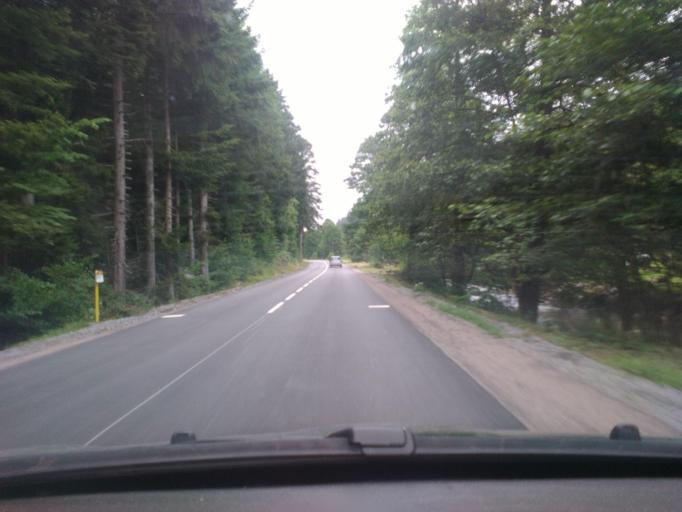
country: FR
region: Lorraine
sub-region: Departement des Vosges
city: Gerardmer
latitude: 48.1178
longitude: 6.8447
